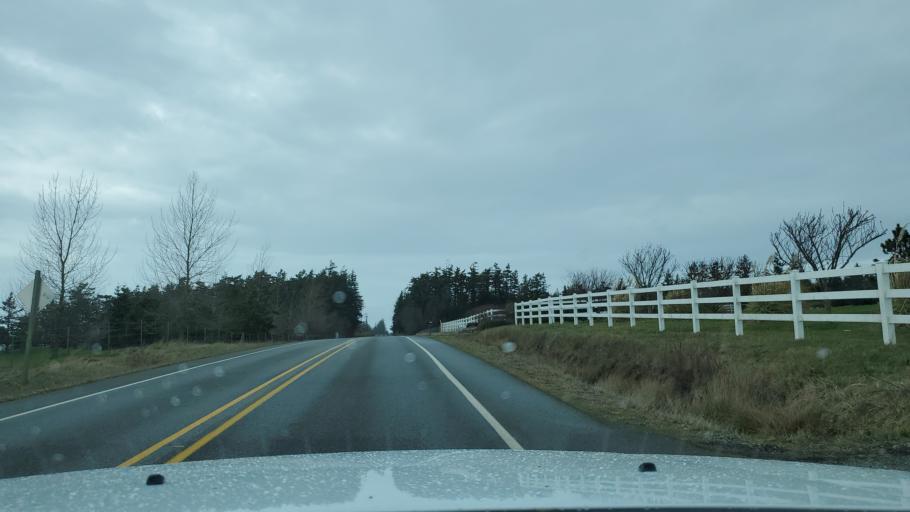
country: US
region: Washington
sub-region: Island County
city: Ault Field
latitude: 48.3122
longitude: -122.6912
